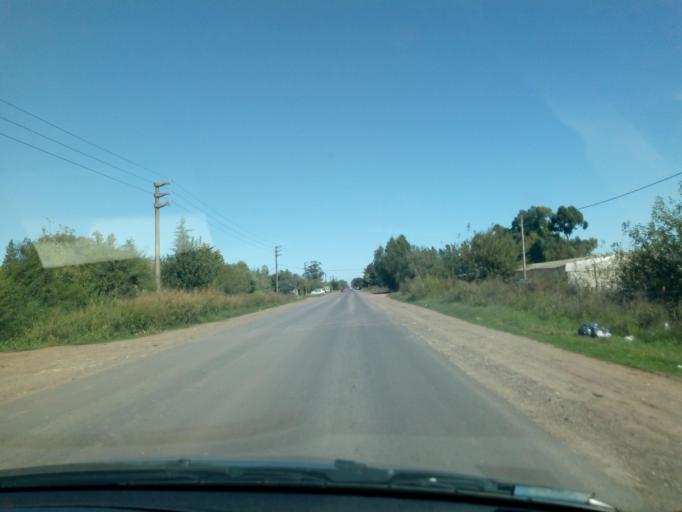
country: AR
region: Buenos Aires
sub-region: Partido de La Plata
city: La Plata
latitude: -35.0075
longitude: -58.0244
